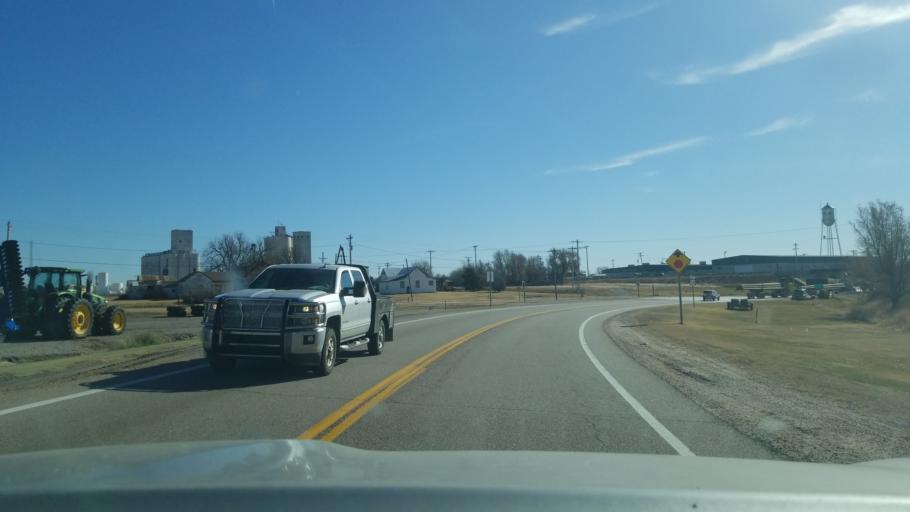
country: US
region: Kansas
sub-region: Kiowa County
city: Greensburg
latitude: 37.5535
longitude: -99.6376
